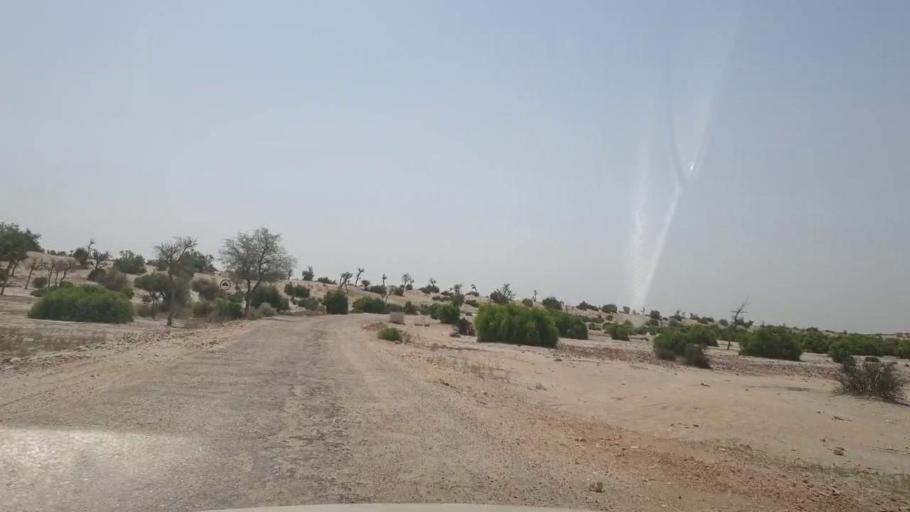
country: PK
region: Sindh
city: Khanpur
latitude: 27.3582
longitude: 69.3169
